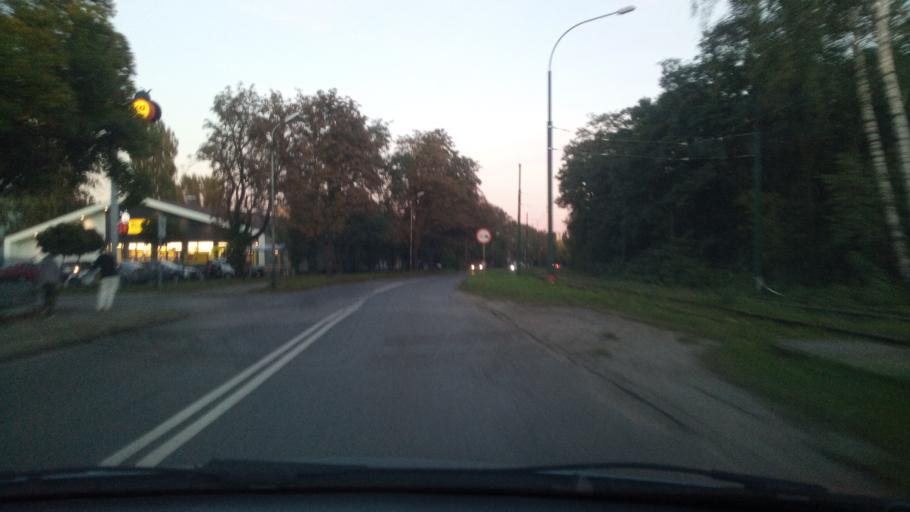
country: PL
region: Silesian Voivodeship
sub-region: Sosnowiec
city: Sosnowiec
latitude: 50.2900
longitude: 19.0942
